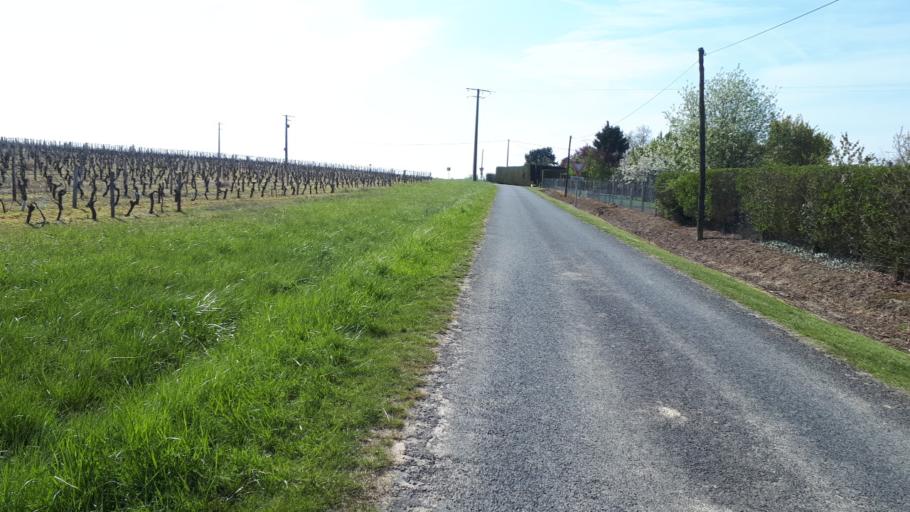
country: FR
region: Centre
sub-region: Departement du Loir-et-Cher
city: Saint-Romain-sur-Cher
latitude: 47.3673
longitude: 1.3900
